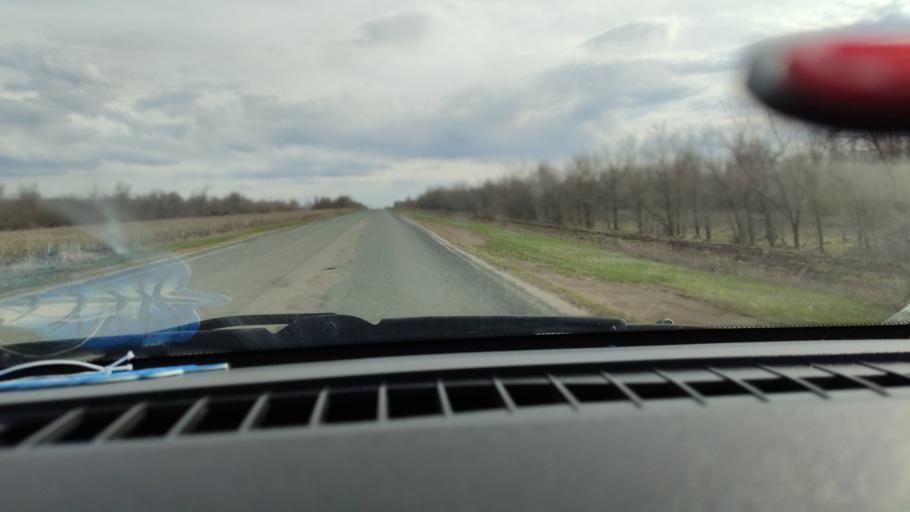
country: RU
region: Saratov
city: Rovnoye
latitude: 50.9699
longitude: 46.1170
